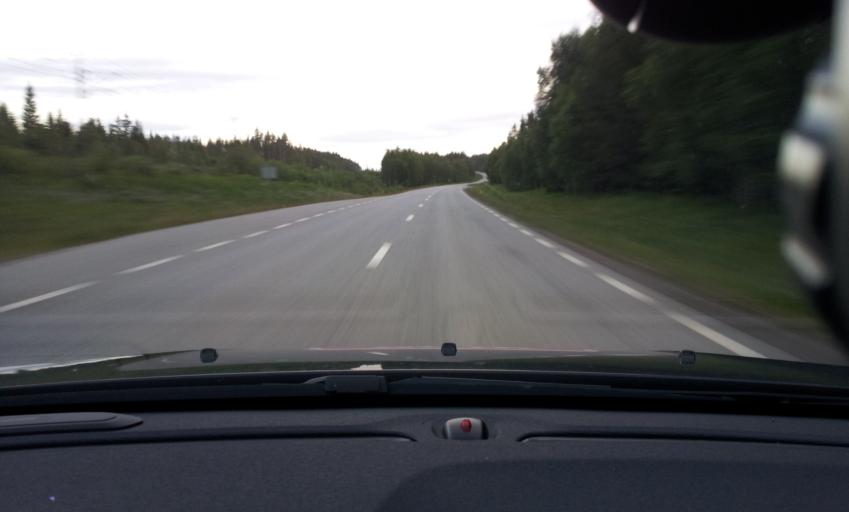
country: SE
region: Jaemtland
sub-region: Ragunda Kommun
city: Hammarstrand
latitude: 63.0306
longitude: 16.3426
